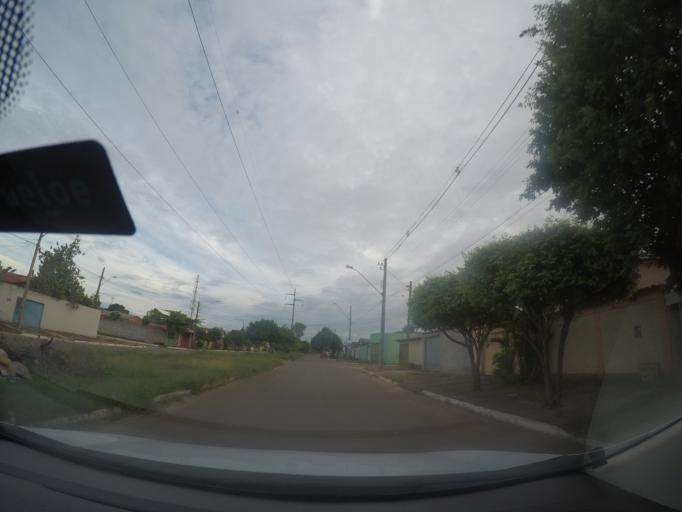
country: BR
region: Goias
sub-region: Goianira
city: Goianira
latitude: -16.5872
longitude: -49.3770
